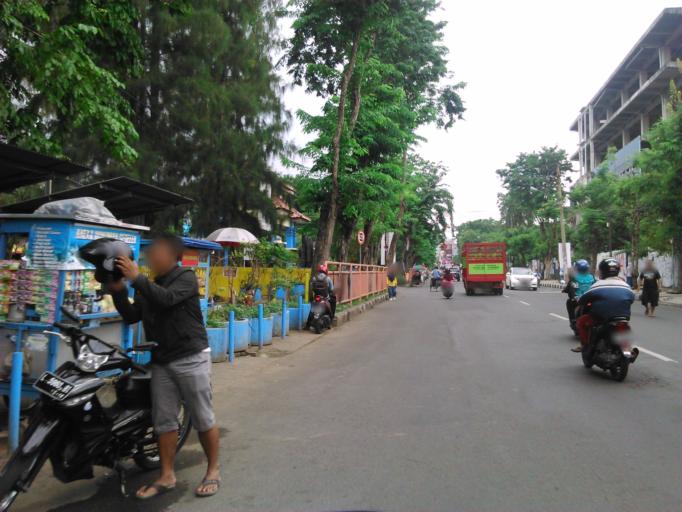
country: ID
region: East Java
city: Gubengairlangga
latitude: -7.2706
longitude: 112.7585
